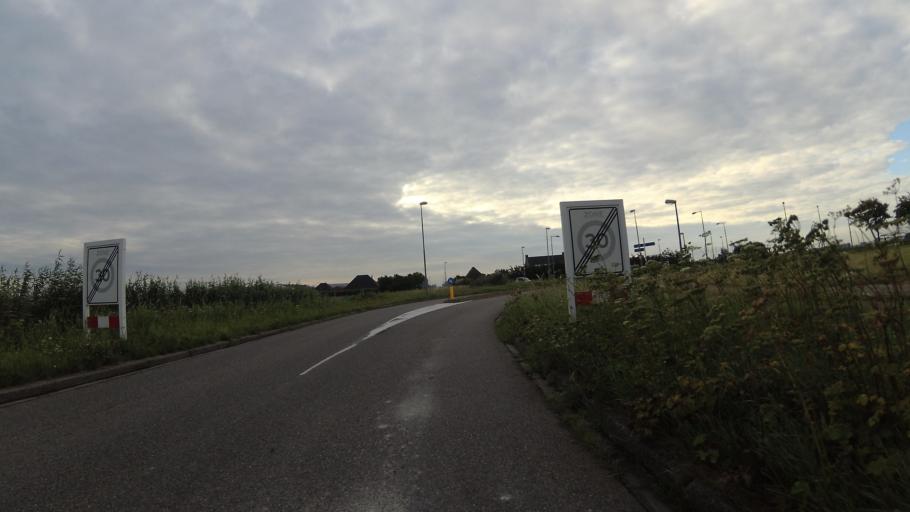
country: NL
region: North Holland
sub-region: Gemeente Den Helder
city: Den Helder
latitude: 52.8964
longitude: 4.7656
